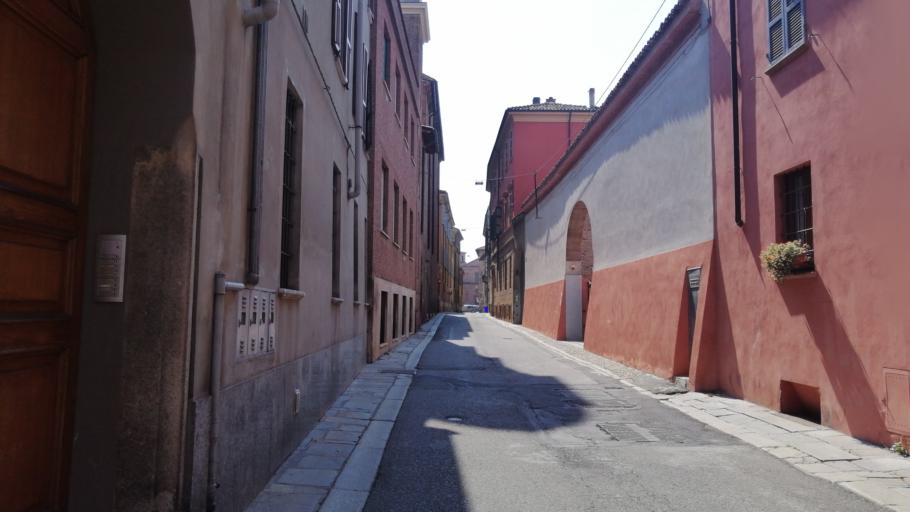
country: IT
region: Emilia-Romagna
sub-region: Provincia di Piacenza
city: Piacenza
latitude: 45.0533
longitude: 9.6973
